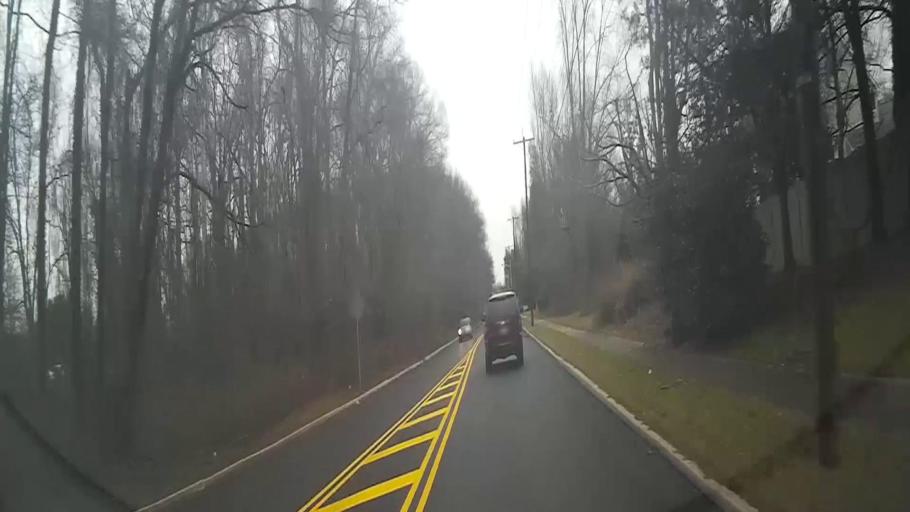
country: US
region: New Jersey
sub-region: Burlington County
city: Marlton
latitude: 39.8679
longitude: -74.9413
